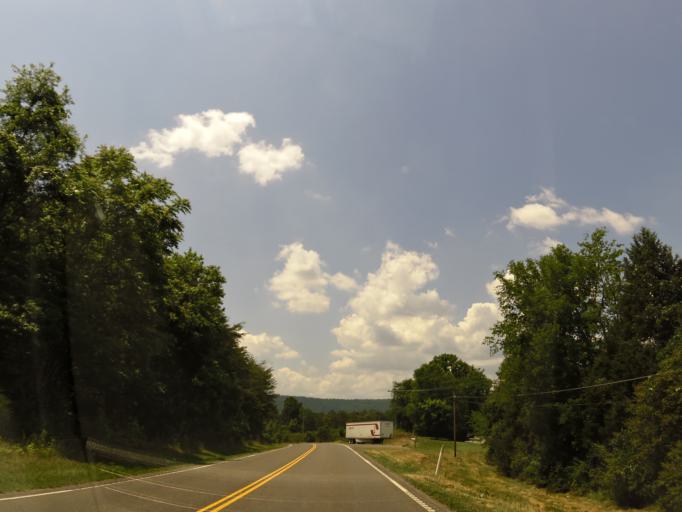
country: US
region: Tennessee
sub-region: Rhea County
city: Spring City
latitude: 35.6507
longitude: -84.8694
